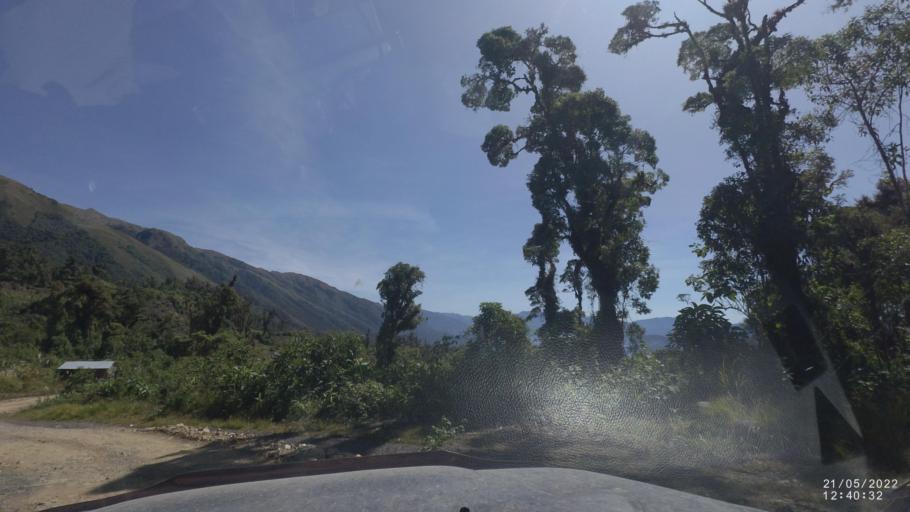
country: BO
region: Cochabamba
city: Colomi
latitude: -17.1961
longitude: -65.9259
